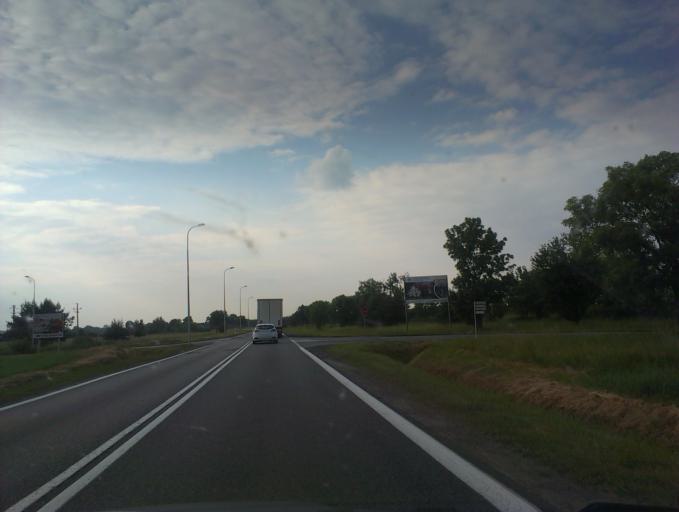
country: PL
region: Lower Silesian Voivodeship
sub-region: Powiat trzebnicki
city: Prusice
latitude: 51.3763
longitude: 16.9495
